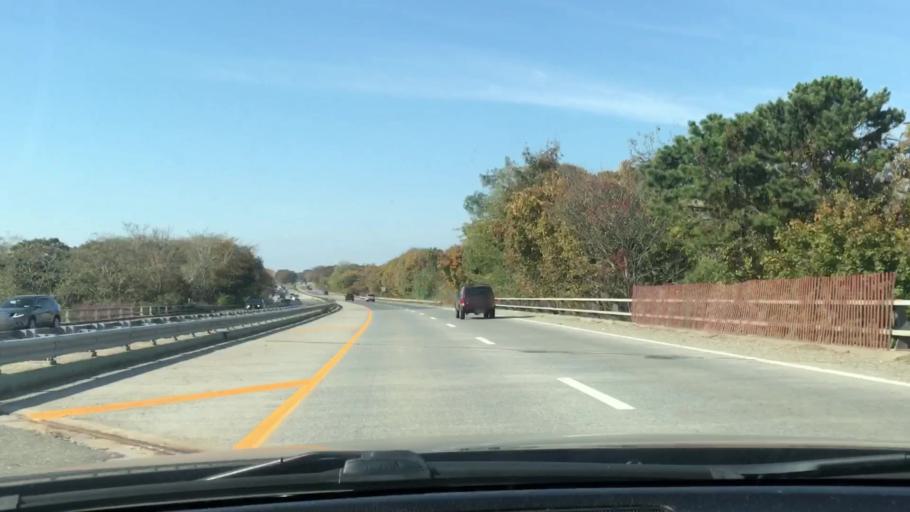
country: US
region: New York
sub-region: Suffolk County
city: Hampton Bays
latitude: 40.8907
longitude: -72.4977
